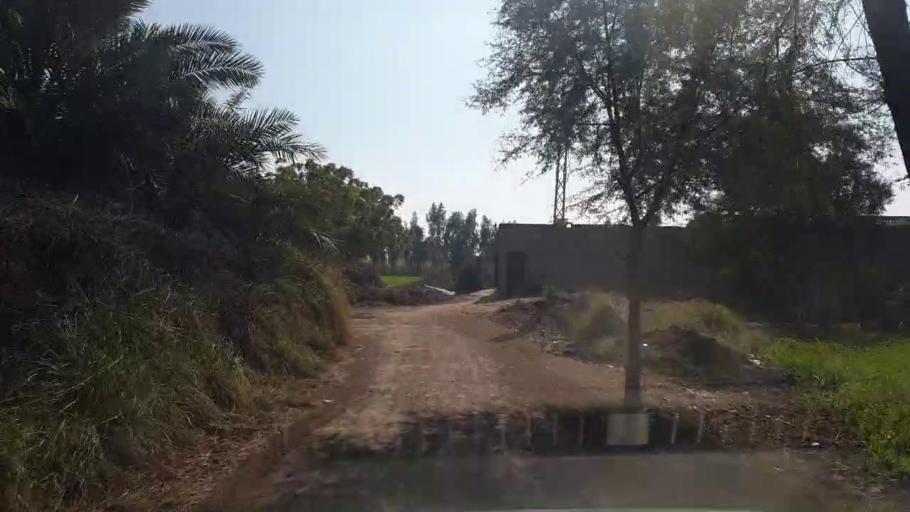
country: PK
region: Sindh
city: Shahdadpur
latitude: 25.9258
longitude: 68.5764
